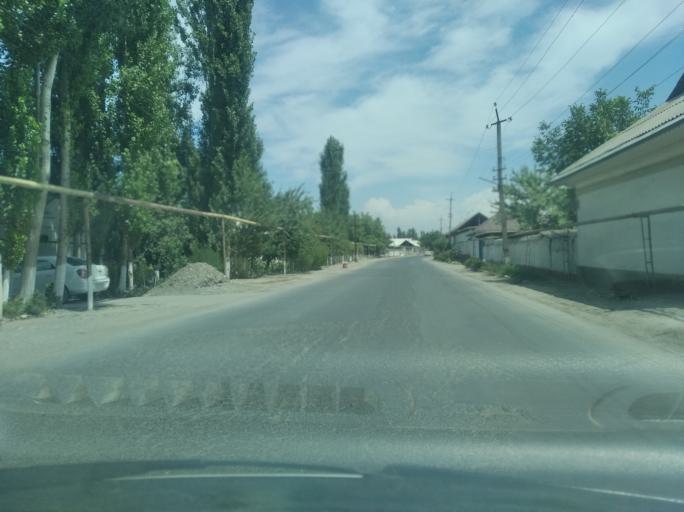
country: UZ
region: Andijon
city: Khujaobod
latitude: 40.6263
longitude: 72.4500
